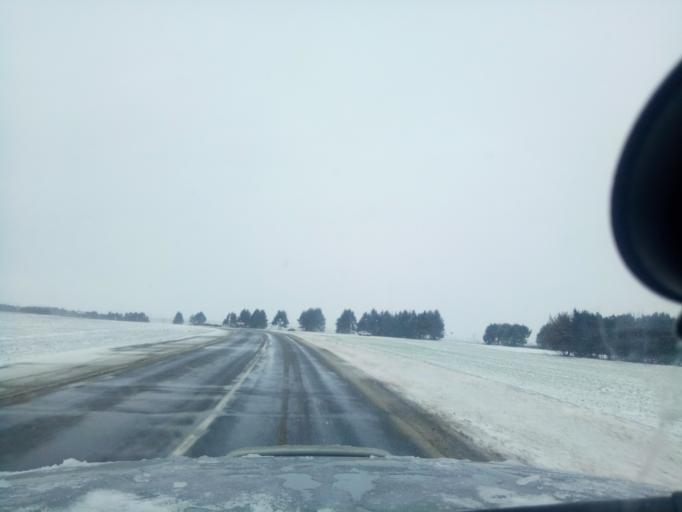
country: BY
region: Minsk
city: Haradzyeya
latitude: 53.2955
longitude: 26.5751
